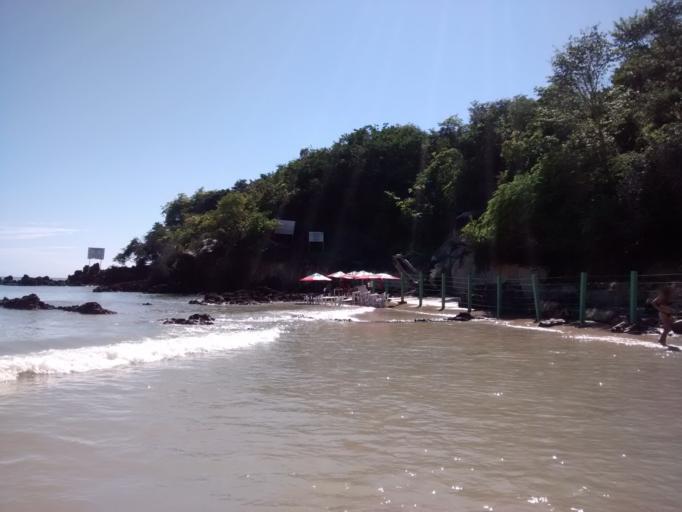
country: BR
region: Rio Grande do Norte
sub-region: Natal
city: Natal
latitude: -5.8836
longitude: -35.1646
